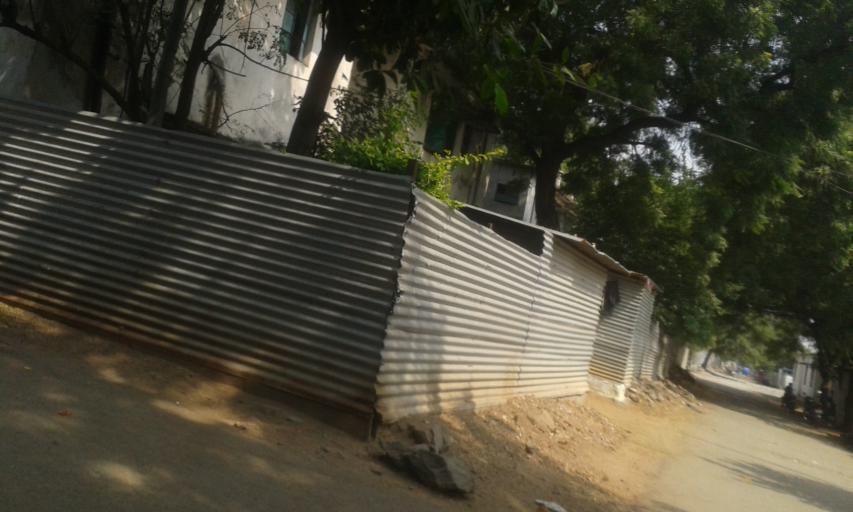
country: IN
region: Karnataka
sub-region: Raichur
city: Lingsugur
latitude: 16.1920
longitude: 76.6617
